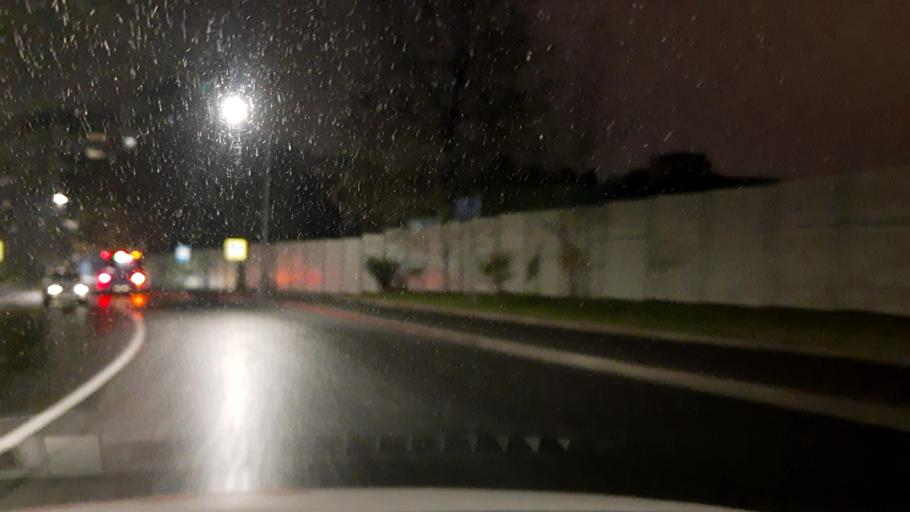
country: RU
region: Moskovskaya
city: Alekseyevka
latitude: 55.6333
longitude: 37.8037
